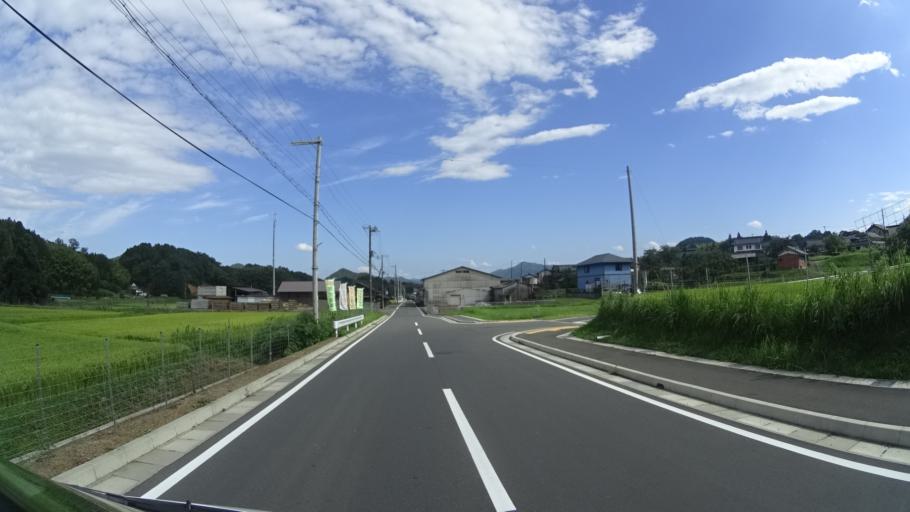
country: JP
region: Kyoto
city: Fukuchiyama
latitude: 35.3316
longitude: 135.1724
